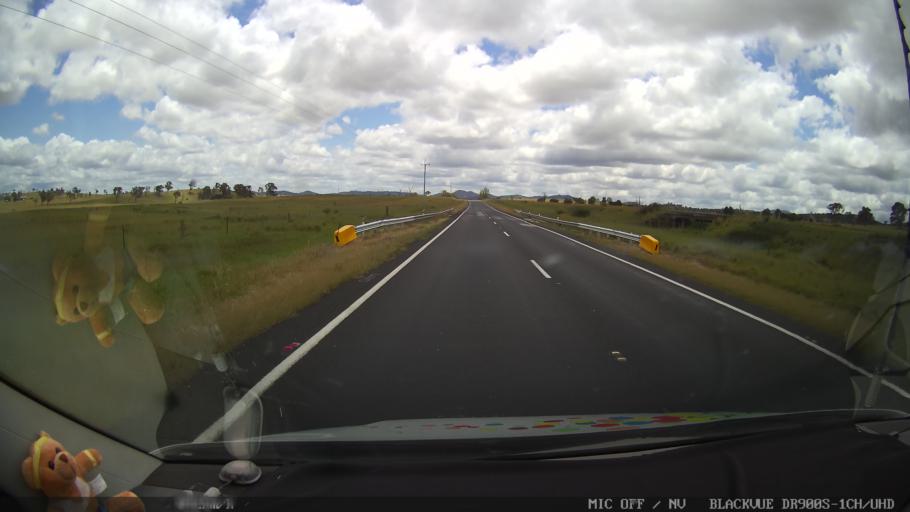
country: AU
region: New South Wales
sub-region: Glen Innes Severn
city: Glen Innes
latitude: -29.4186
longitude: 151.8628
